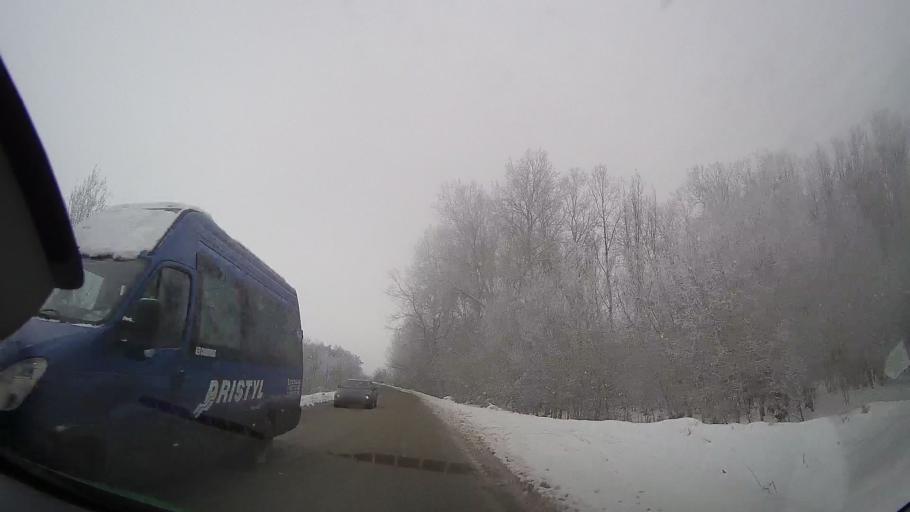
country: RO
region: Neamt
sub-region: Comuna Horia
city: Cotu Vames
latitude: 46.8862
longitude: 26.9688
